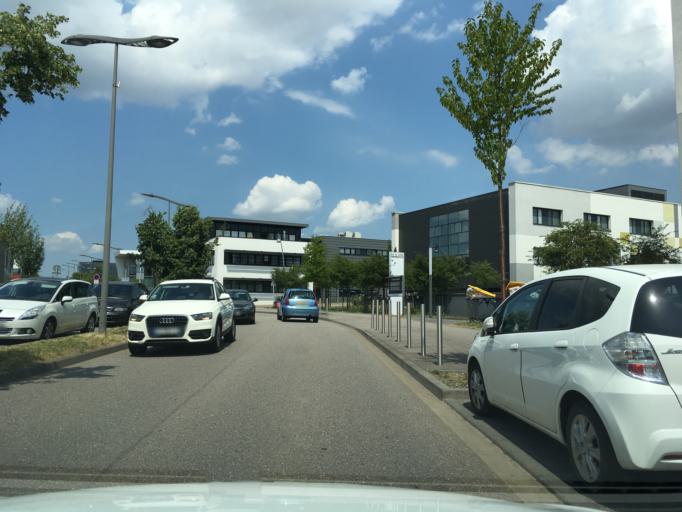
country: FR
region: Lorraine
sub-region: Departement de la Moselle
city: Saint-Julien-les-Metz
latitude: 49.1154
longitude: 6.2328
